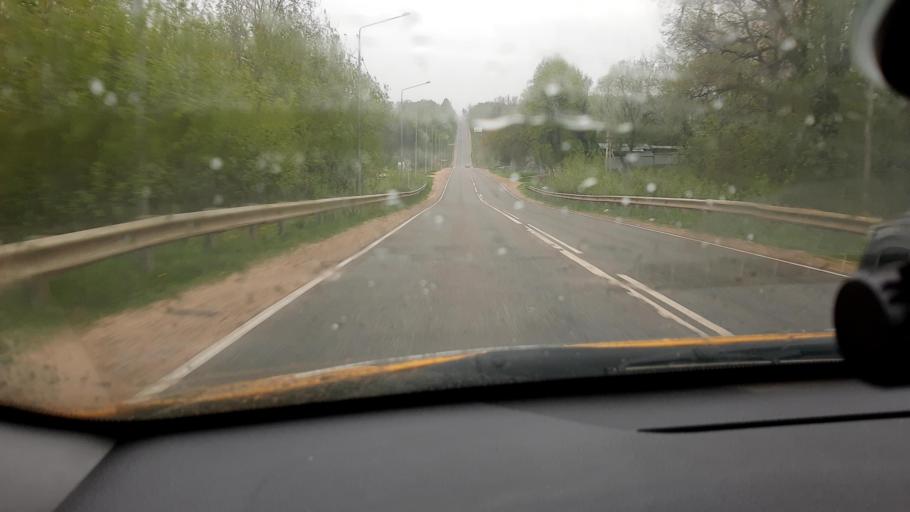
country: RU
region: Tula
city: Zaokskiy
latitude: 54.7586
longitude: 37.4376
